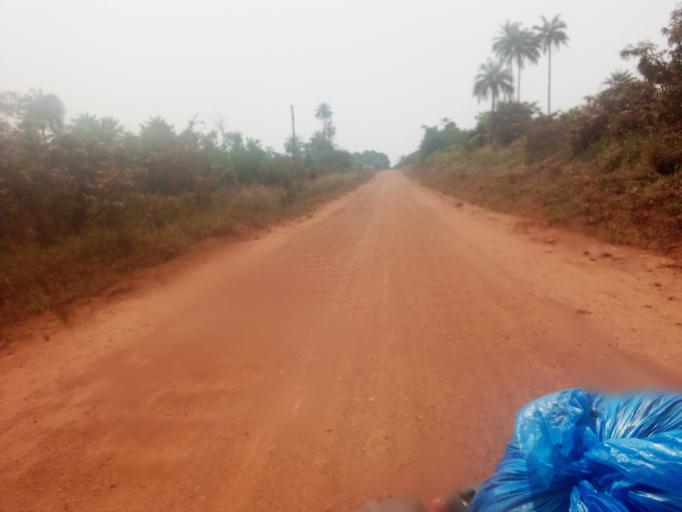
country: SL
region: Southern Province
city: Sumbuya
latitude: 7.6652
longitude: -11.9906
